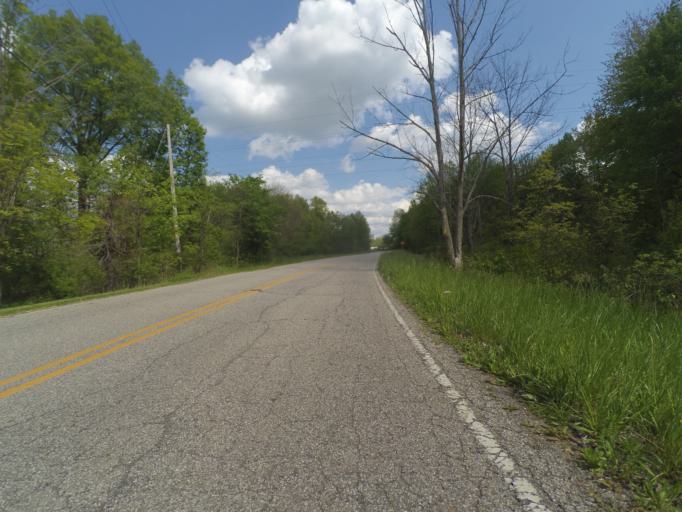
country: US
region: Ohio
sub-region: Trumbull County
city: Lordstown
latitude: 41.1290
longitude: -80.8604
